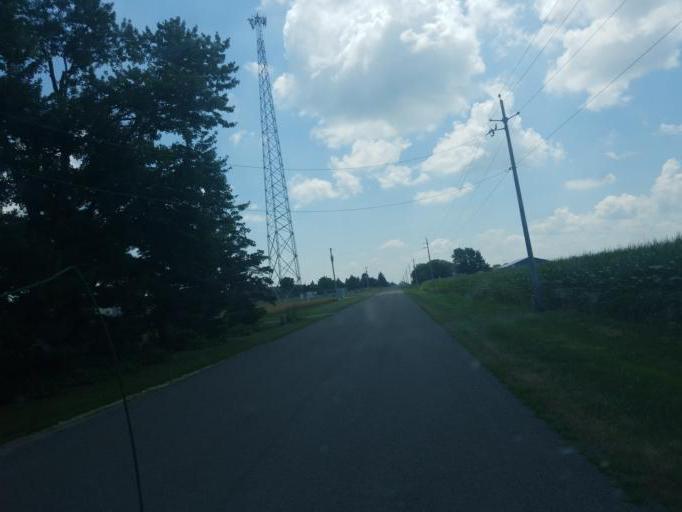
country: US
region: Ohio
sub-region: Mercer County
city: Celina
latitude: 40.5765
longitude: -84.4940
